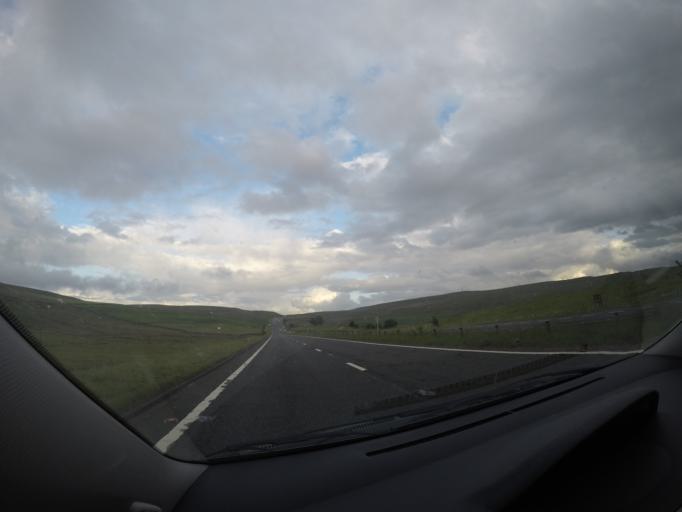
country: GB
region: England
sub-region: County Durham
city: Holwick
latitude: 54.5197
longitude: -2.2172
